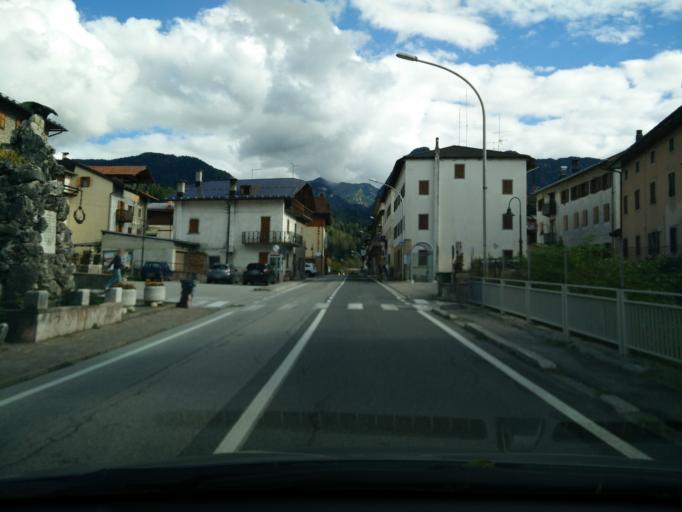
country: IT
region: Veneto
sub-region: Provincia di Belluno
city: Lorenzago di Cadore
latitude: 46.4892
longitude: 12.4602
